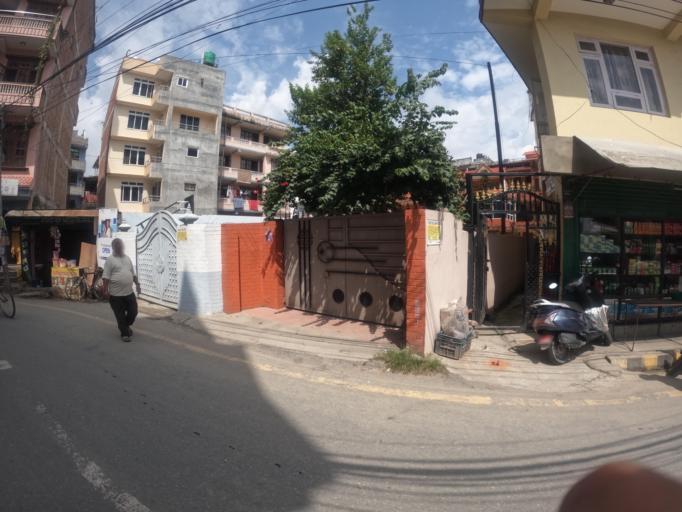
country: NP
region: Central Region
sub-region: Bagmati Zone
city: Kathmandu
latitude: 27.6784
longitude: 85.3622
